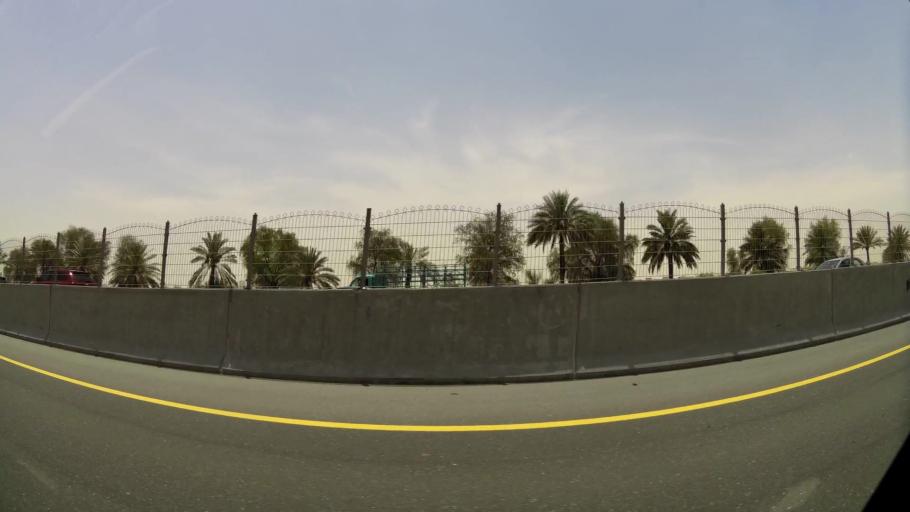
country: AE
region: Dubai
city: Dubai
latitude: 25.1090
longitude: 55.3432
